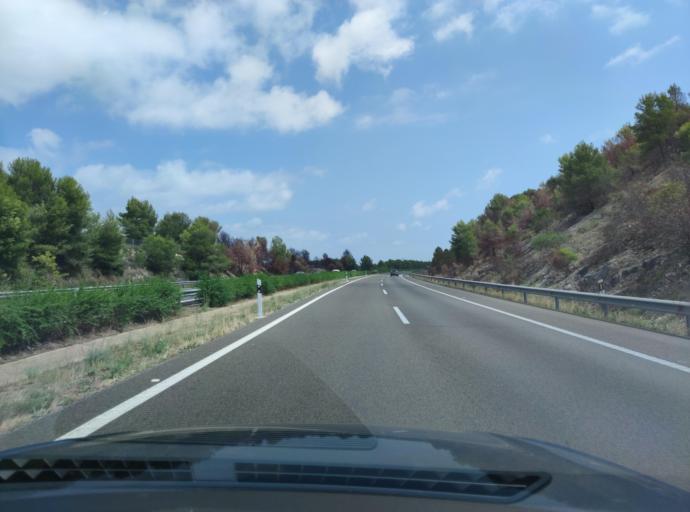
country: ES
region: Valencia
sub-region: Provincia de Castello
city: Santa Magdalena de Pulpis
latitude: 40.3858
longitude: 0.3454
